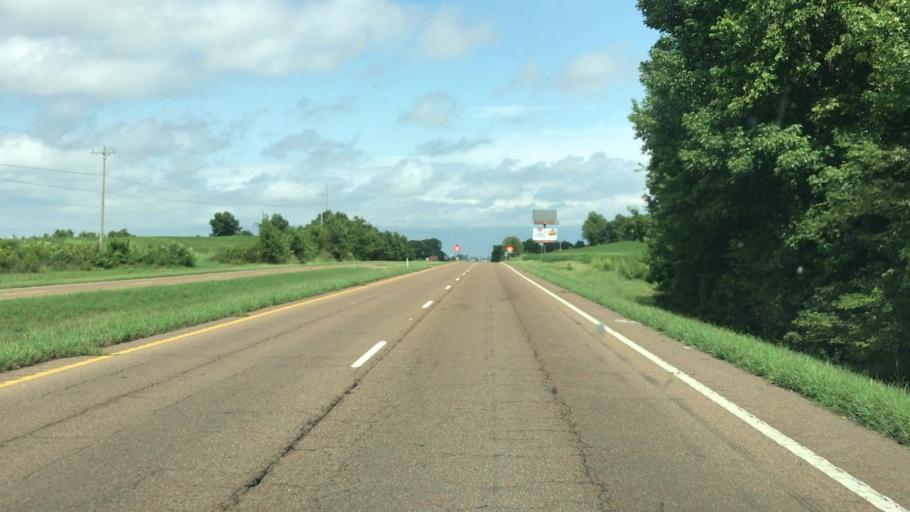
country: US
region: Tennessee
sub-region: Obion County
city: Englewood
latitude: 36.3809
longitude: -89.1116
